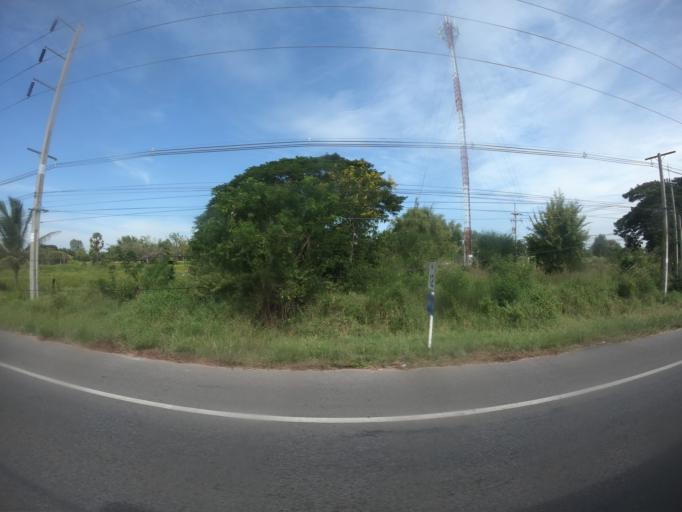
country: TH
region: Maha Sarakham
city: Chiang Yuen
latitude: 16.4455
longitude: 103.0263
